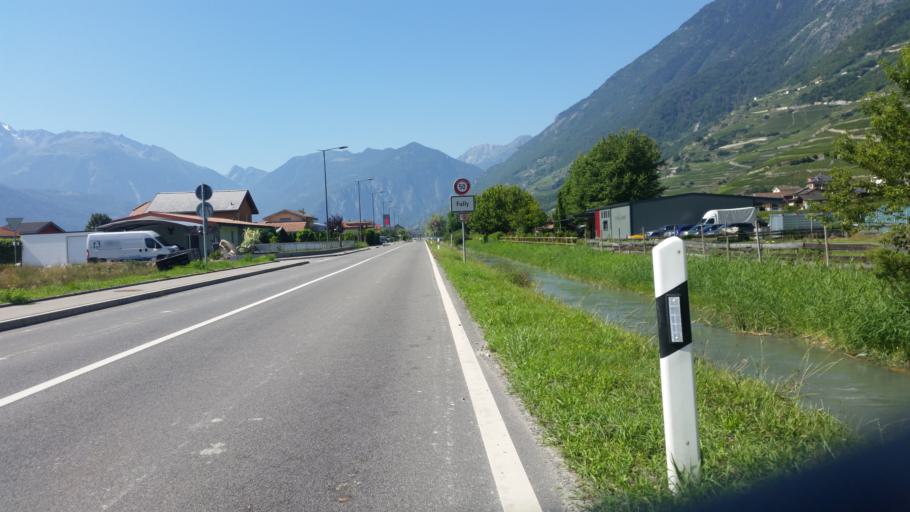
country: CH
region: Valais
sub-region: Martigny District
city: Charrat-les-Chenes
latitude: 46.1516
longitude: 7.1438
